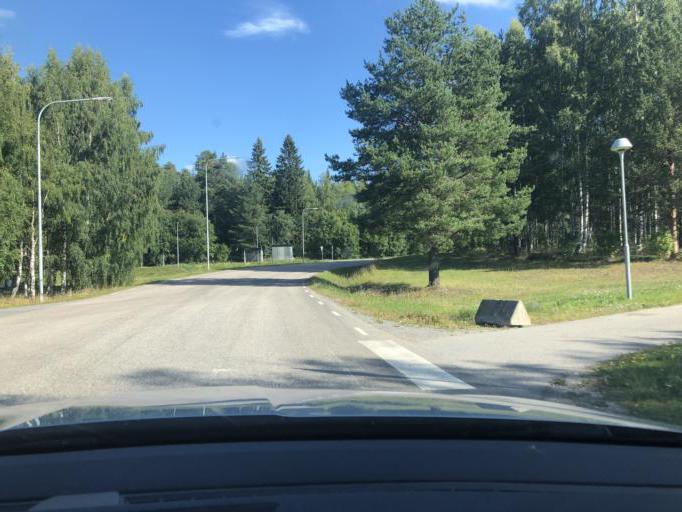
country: SE
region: Vaesternorrland
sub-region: Sundsvalls Kommun
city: Sundsvall
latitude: 62.4099
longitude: 17.3018
